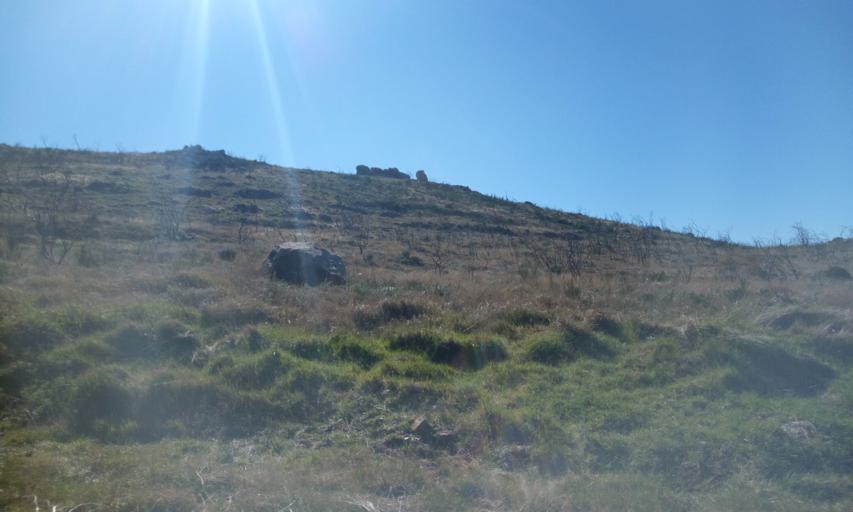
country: PT
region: Guarda
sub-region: Manteigas
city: Manteigas
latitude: 40.4881
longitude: -7.5653
